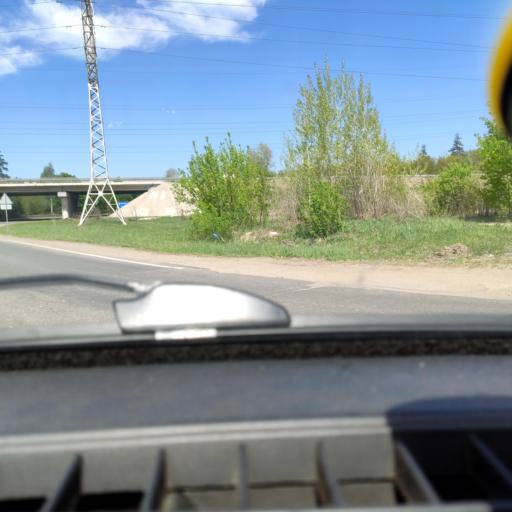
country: RU
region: Samara
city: Pribrezhnyy
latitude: 53.5166
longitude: 49.8351
